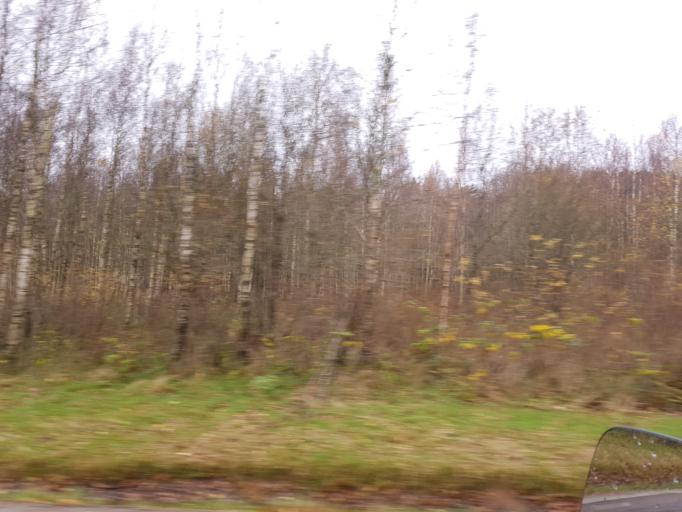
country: SE
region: Vaestra Goetaland
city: Svanesund
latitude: 58.1644
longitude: 11.8203
